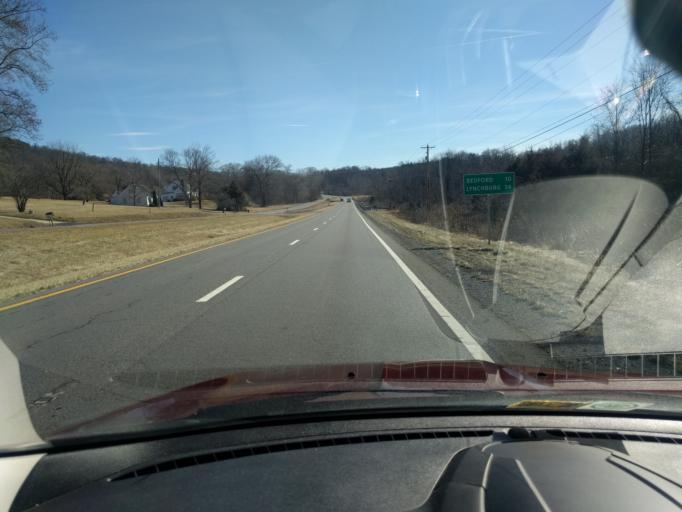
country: US
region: Virginia
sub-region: Botetourt County
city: Blue Ridge
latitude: 37.3733
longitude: -79.7023
